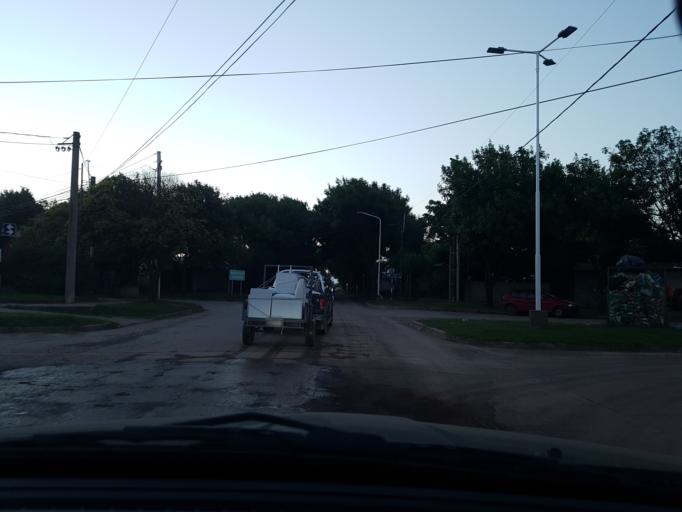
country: AR
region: Cordoba
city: General Cabrera
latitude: -32.7608
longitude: -63.7982
